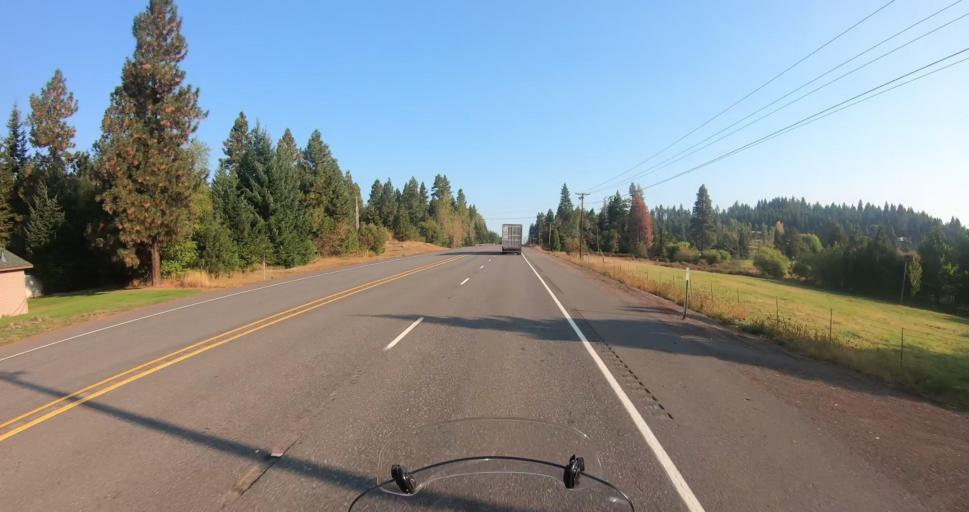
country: US
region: Oregon
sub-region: Hood River County
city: Odell
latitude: 45.5751
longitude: -121.5548
